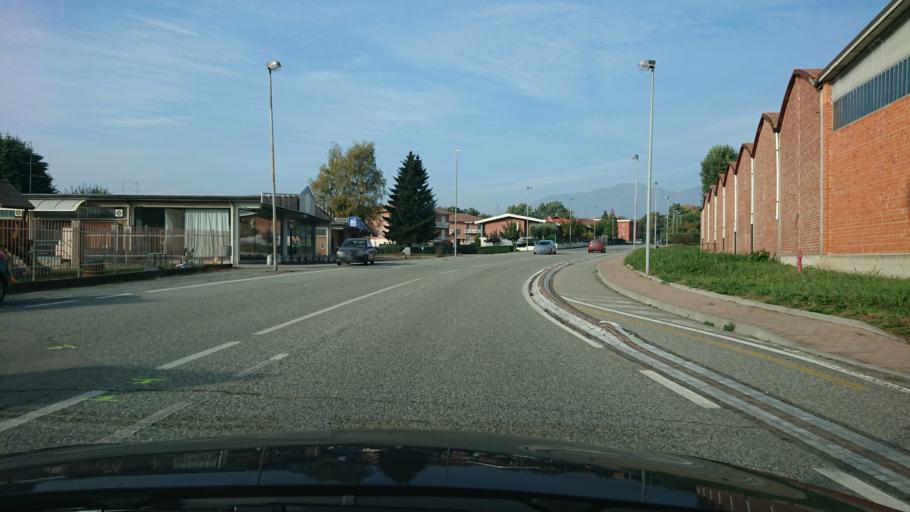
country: IT
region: Piedmont
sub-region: Provincia di Biella
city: Vigliano Biellese
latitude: 45.5601
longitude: 8.1081
